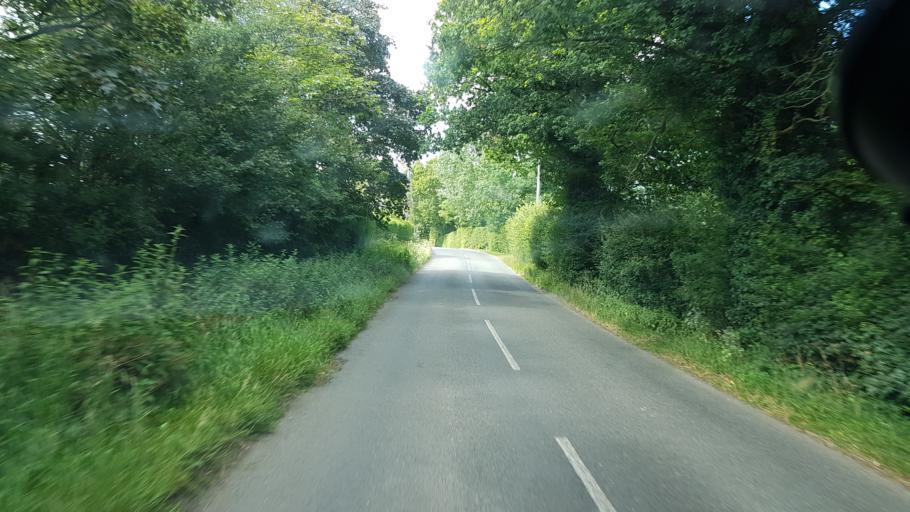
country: GB
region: England
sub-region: West Sussex
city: Rudgwick
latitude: 51.0661
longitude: -0.4471
